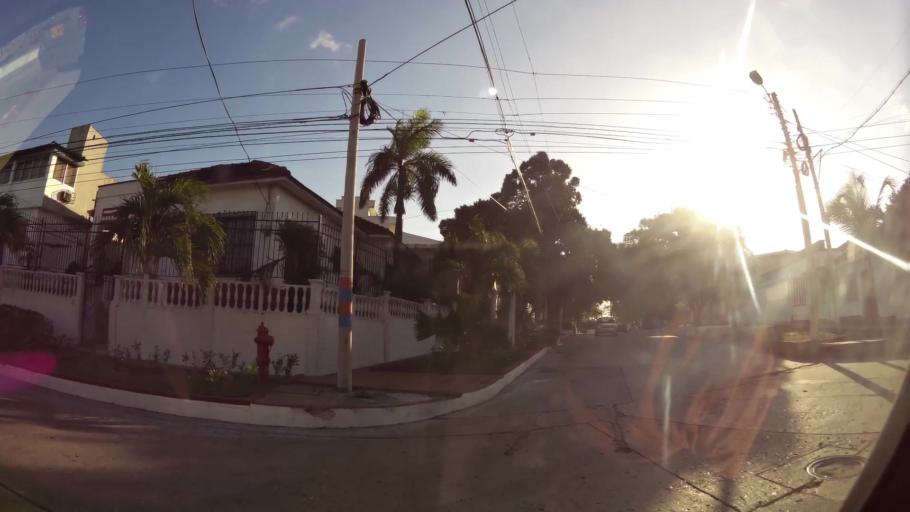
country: CO
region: Atlantico
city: Barranquilla
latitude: 10.9832
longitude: -74.8004
